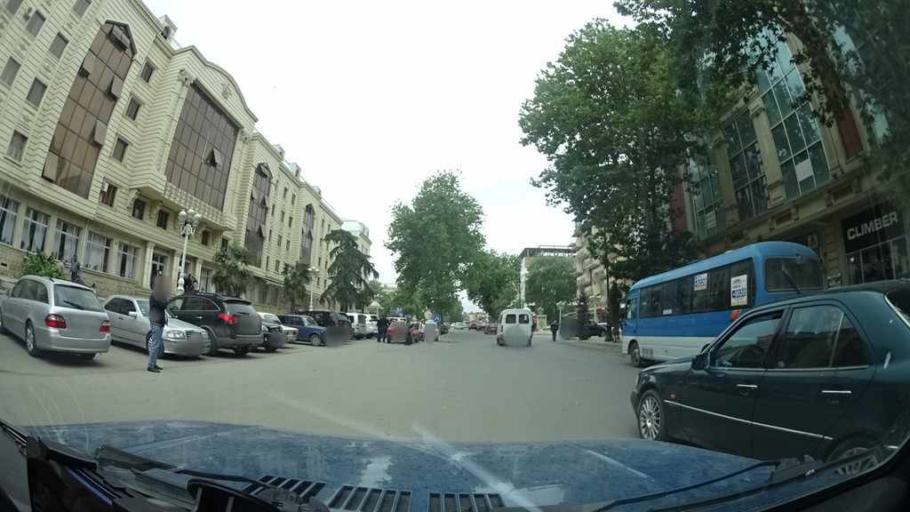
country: AZ
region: Ganja City
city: Ganja
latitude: 40.6810
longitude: 46.3602
